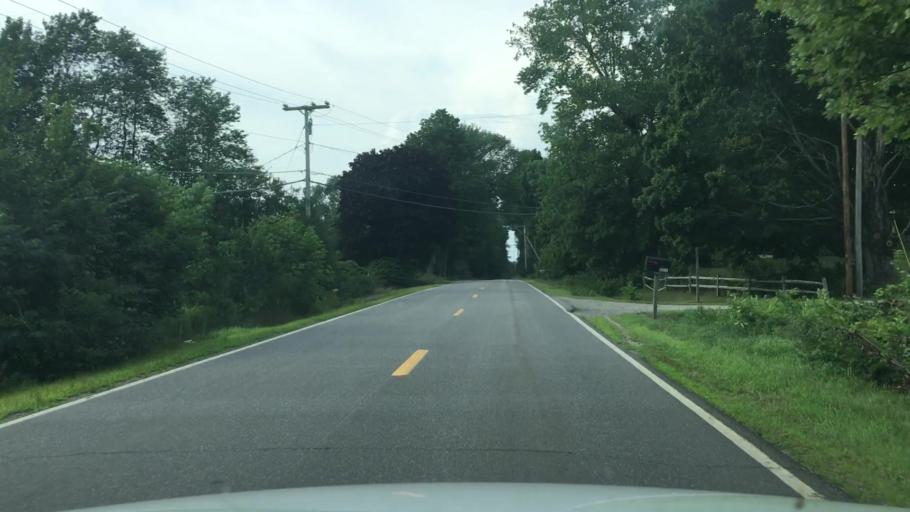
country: US
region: Maine
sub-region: Lincoln County
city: Waldoboro
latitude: 44.1335
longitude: -69.3701
